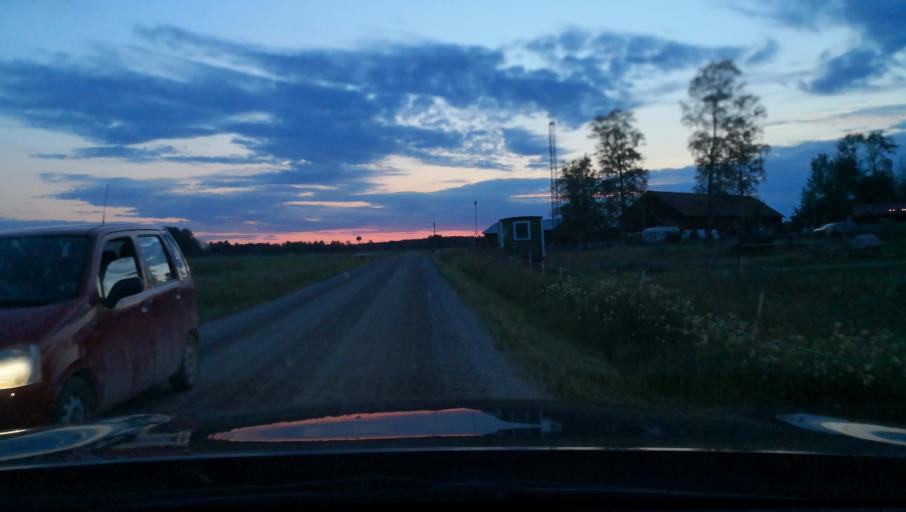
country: SE
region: Uppsala
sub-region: Osthammars Kommun
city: Bjorklinge
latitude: 60.0076
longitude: 17.3306
